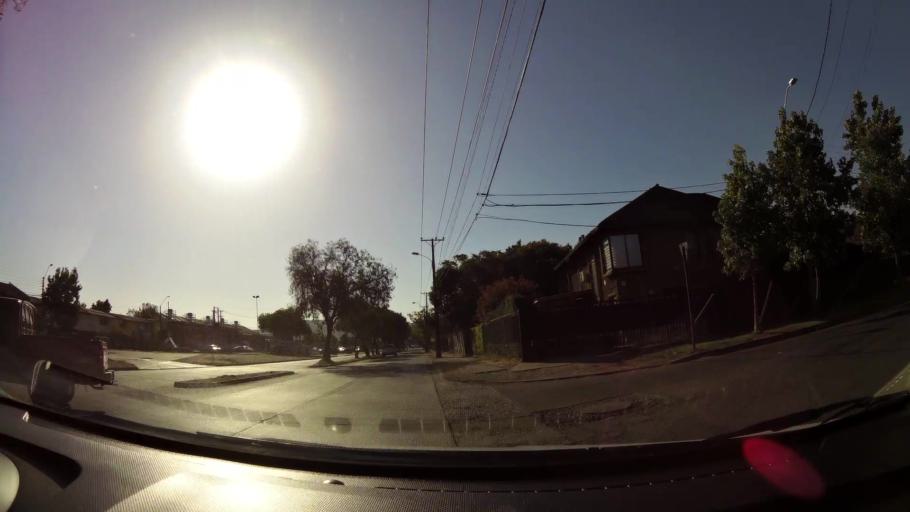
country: CL
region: Maule
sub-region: Provincia de Talca
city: Talca
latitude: -35.4393
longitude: -71.6800
